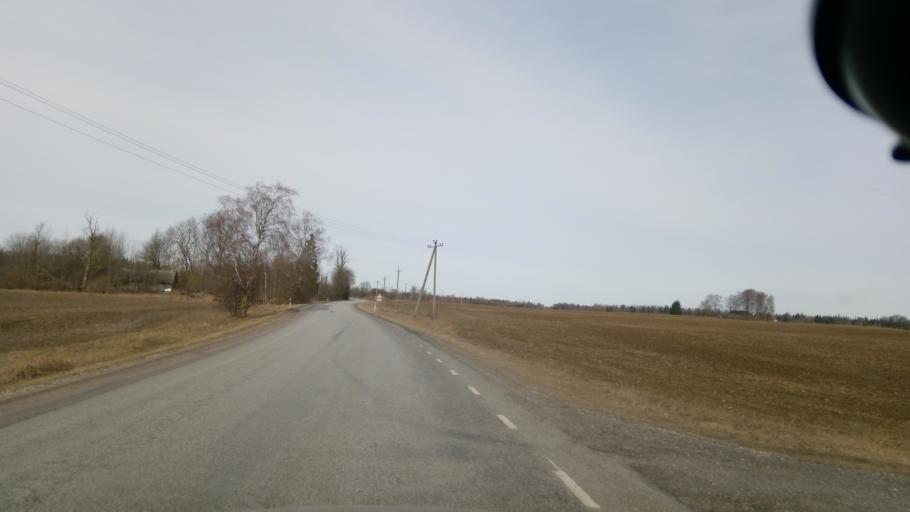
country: EE
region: Raplamaa
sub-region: Rapla vald
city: Rapla
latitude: 59.0282
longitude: 24.8380
